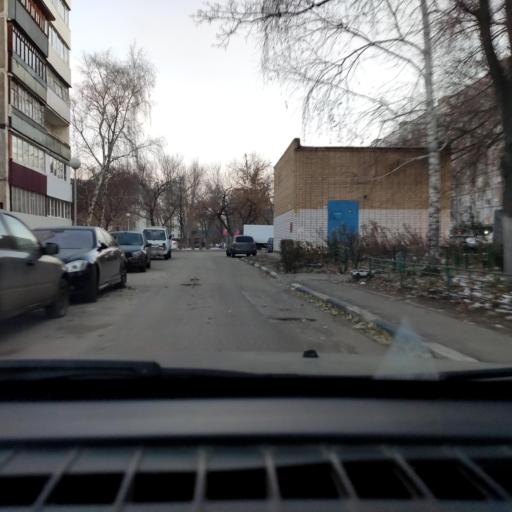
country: RU
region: Samara
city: Tol'yatti
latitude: 53.5337
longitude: 49.2754
